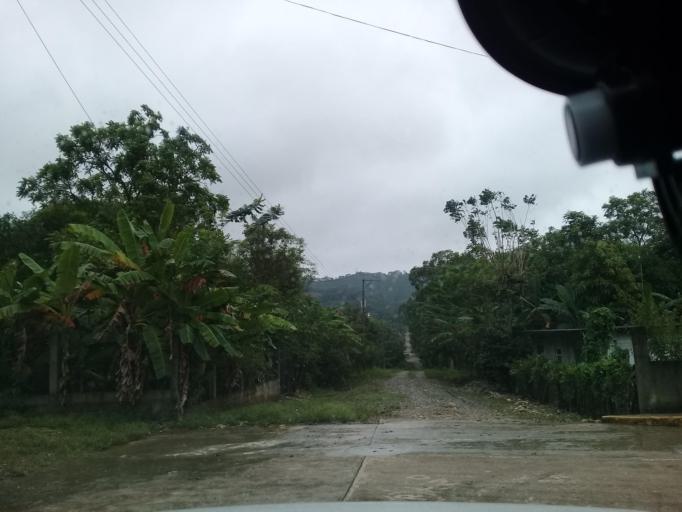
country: MX
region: Veracruz
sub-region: Chalma
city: San Pedro Coyutla
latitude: 21.2257
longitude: -98.4306
